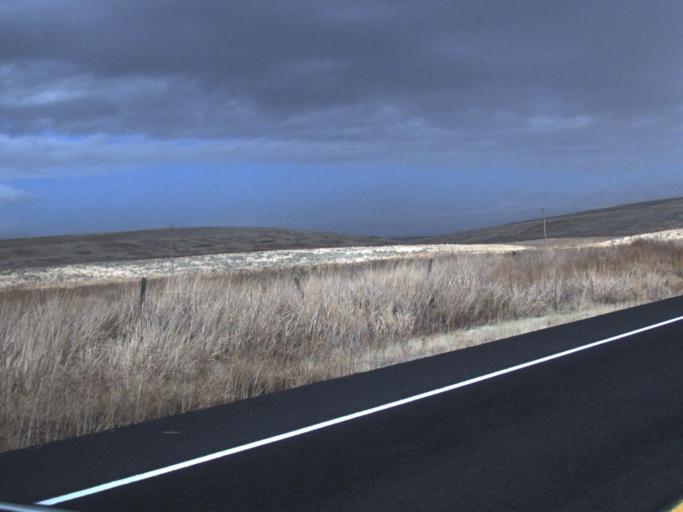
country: US
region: Washington
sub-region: Adams County
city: Ritzville
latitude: 47.3471
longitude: -118.5989
